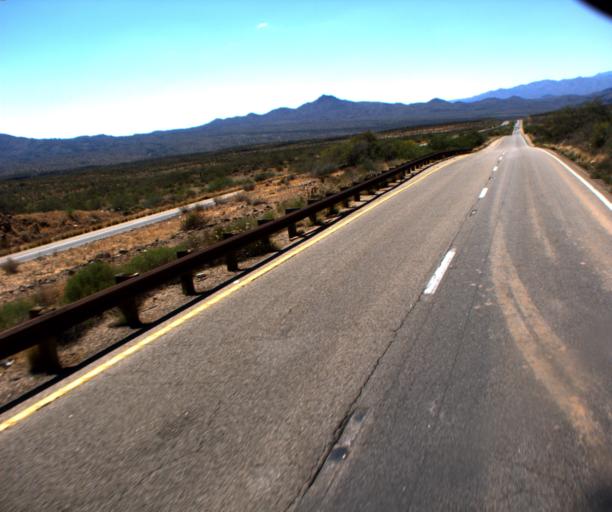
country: US
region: Arizona
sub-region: Yavapai County
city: Bagdad
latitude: 34.4853
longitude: -113.3703
